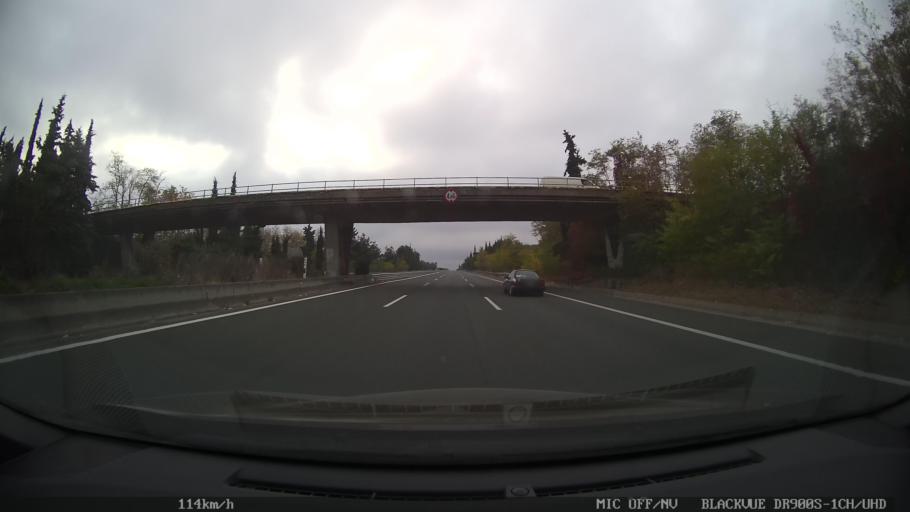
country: GR
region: Central Macedonia
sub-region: Nomos Pierias
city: Makrygialos
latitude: 40.4459
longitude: 22.5821
